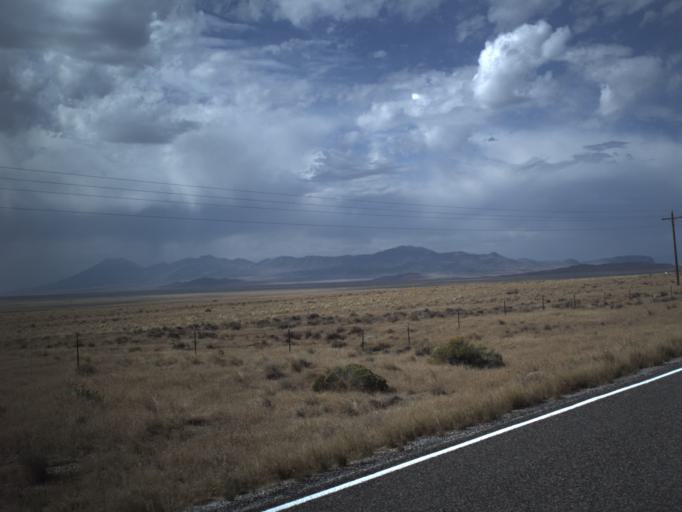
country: US
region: Utah
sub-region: Tooele County
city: Wendover
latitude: 41.4358
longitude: -113.7534
